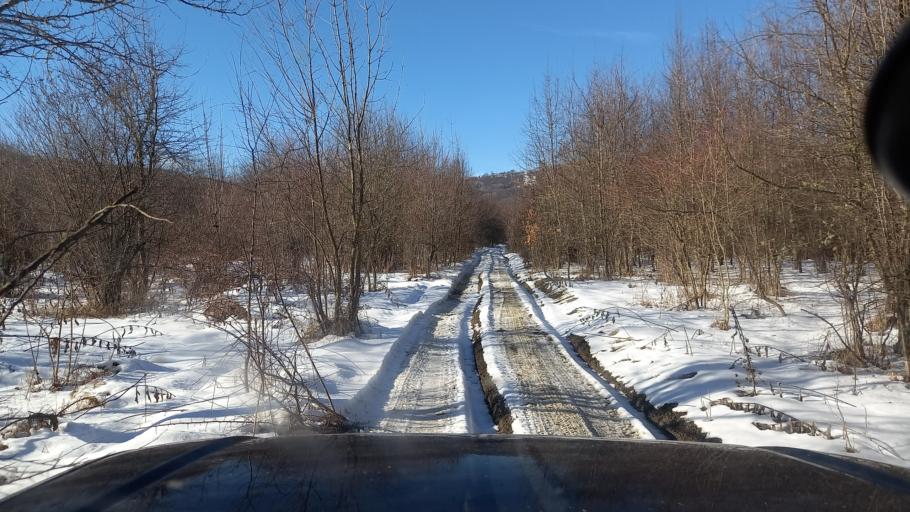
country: RU
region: Adygeya
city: Kamennomostskiy
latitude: 44.2096
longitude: 40.1449
